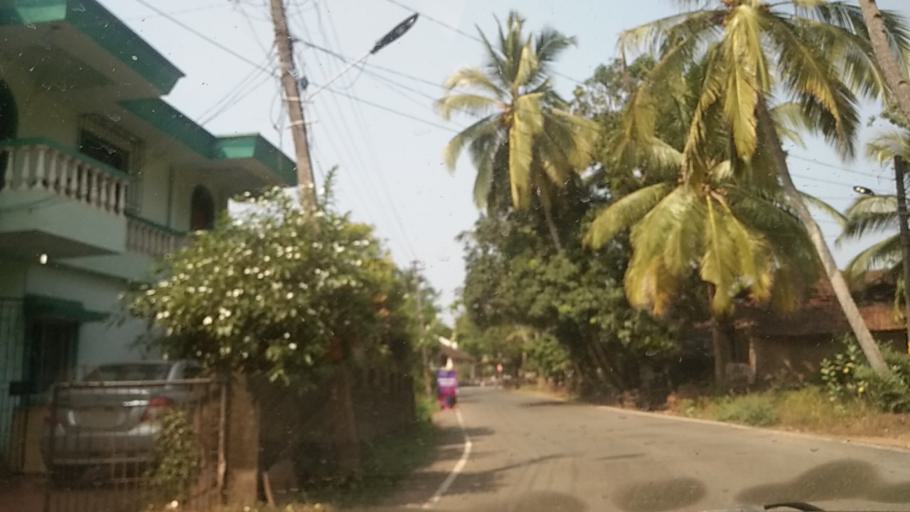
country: IN
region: Goa
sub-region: South Goa
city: Cavelossim
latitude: 15.1565
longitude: 73.9654
